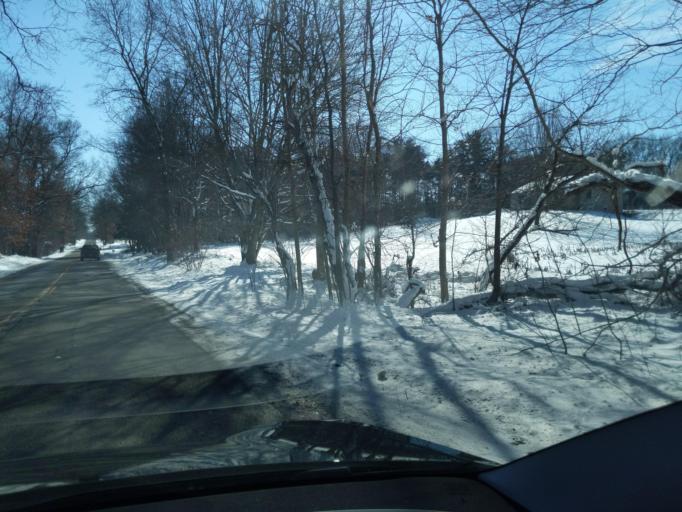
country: US
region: Michigan
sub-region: Ingham County
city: Stockbridge
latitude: 42.4543
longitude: -84.0764
